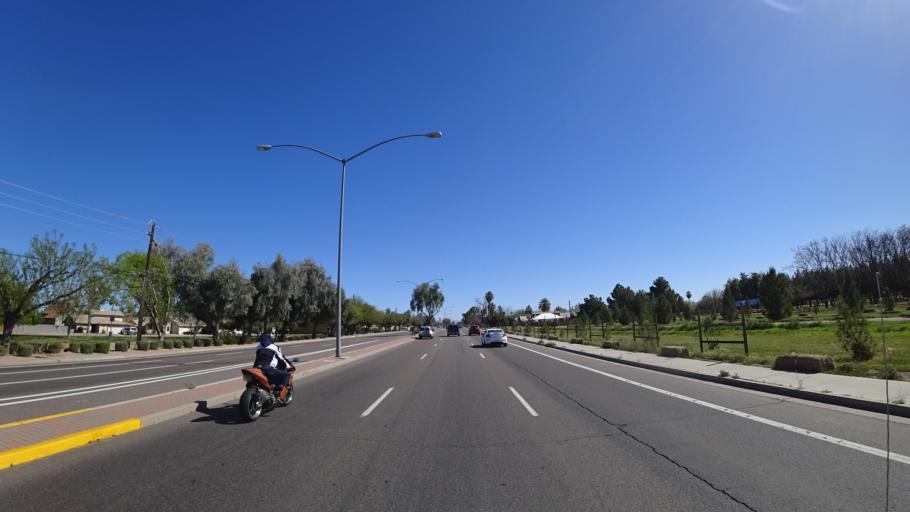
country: US
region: Arizona
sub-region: Maricopa County
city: Gilbert
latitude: 33.3789
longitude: -111.7970
